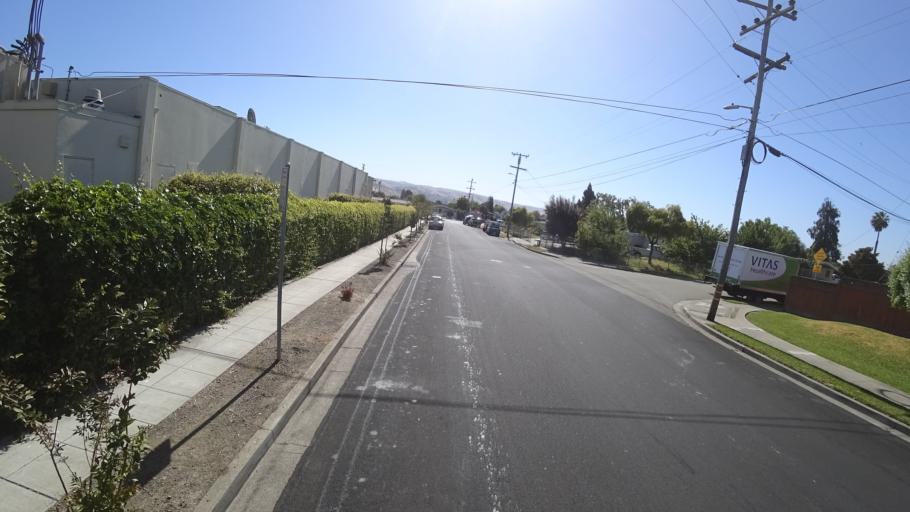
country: US
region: California
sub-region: Alameda County
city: Hayward
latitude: 37.6299
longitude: -122.0768
